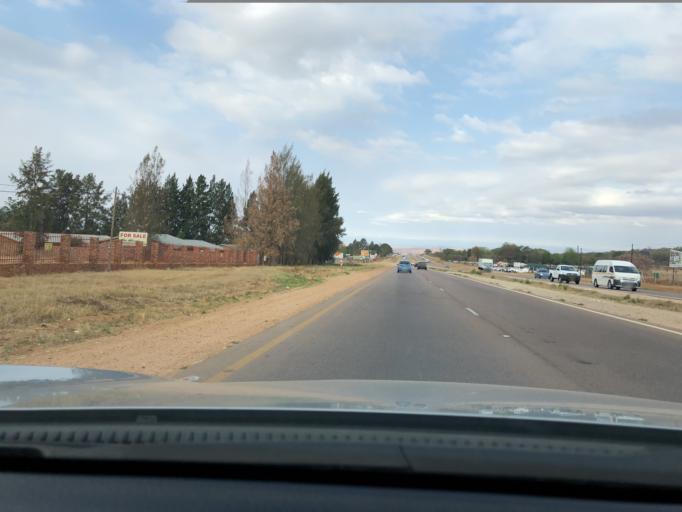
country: ZA
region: Limpopo
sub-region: Capricorn District Municipality
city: Polokwane
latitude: -23.8986
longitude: 29.5254
